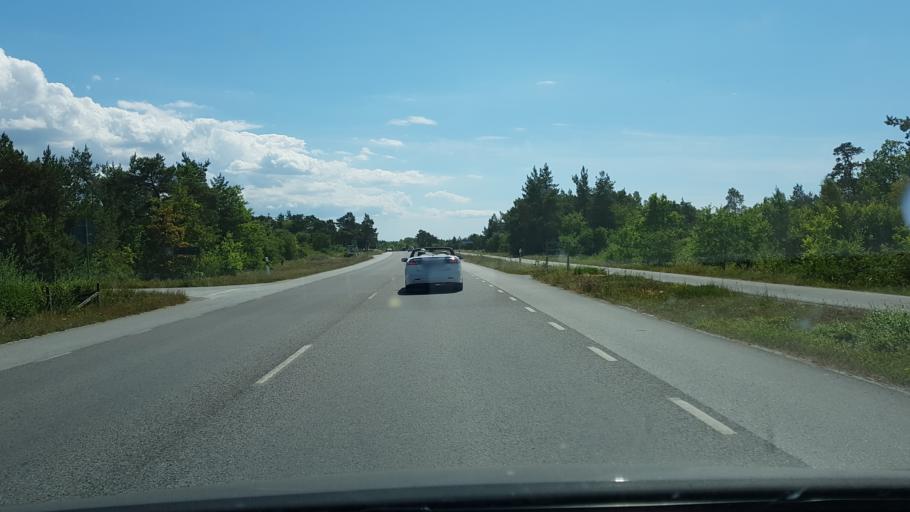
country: SE
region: Gotland
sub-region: Gotland
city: Klintehamn
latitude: 57.5070
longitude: 18.1531
